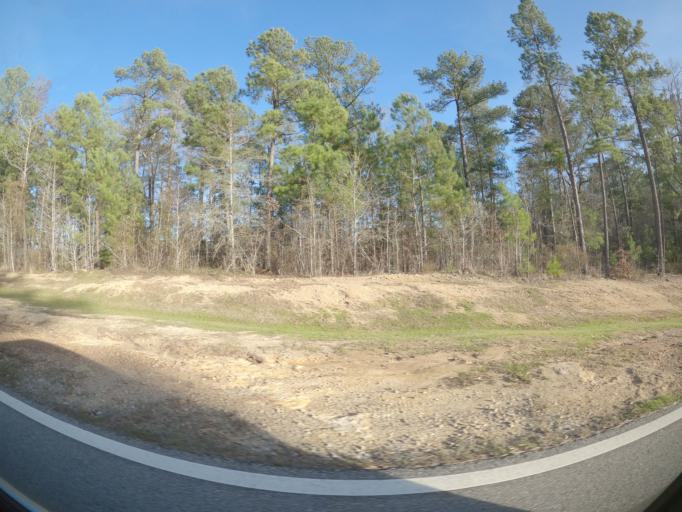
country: US
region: Georgia
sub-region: Columbia County
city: Evans
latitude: 33.5843
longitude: -82.1995
